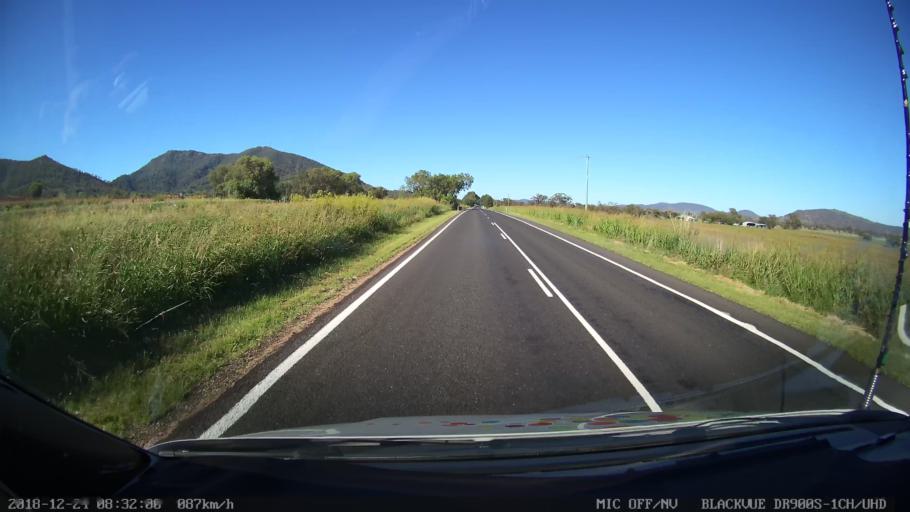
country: AU
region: New South Wales
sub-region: Tamworth Municipality
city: Phillip
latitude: -31.2771
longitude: 150.7040
